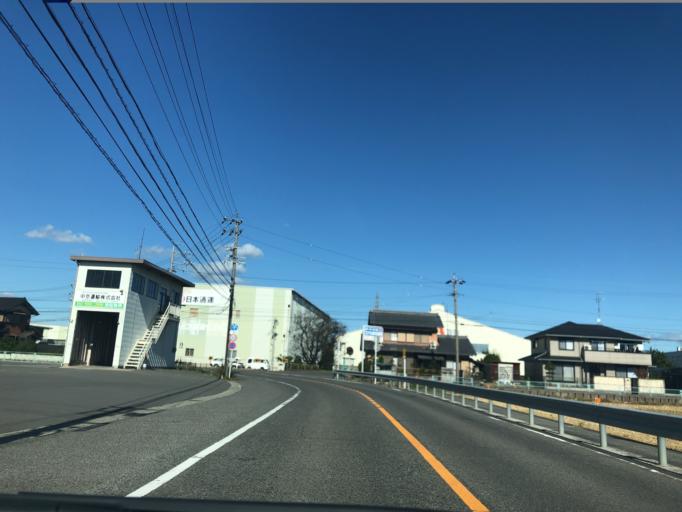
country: JP
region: Gifu
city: Ogaki
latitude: 35.3963
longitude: 136.6658
